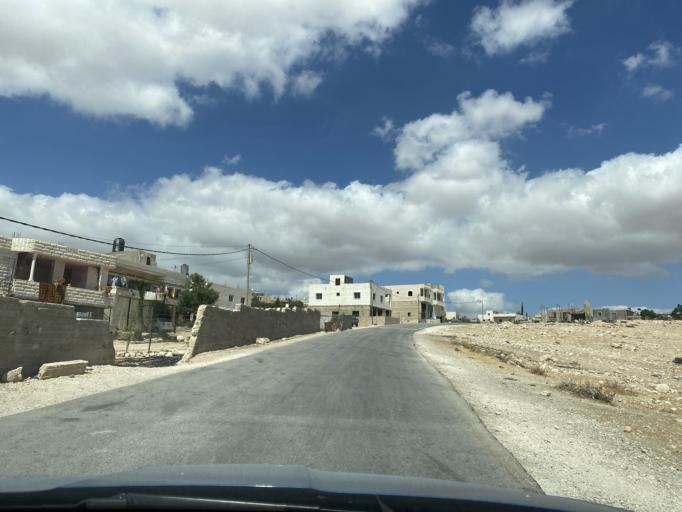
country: PS
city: `Arab ar Rashaydah
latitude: 31.5706
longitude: 35.2340
